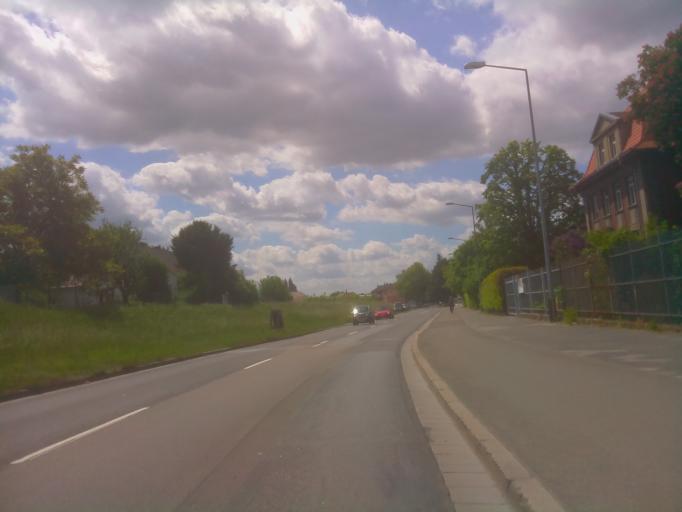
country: DE
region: Rheinland-Pfalz
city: Speyer
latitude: 49.3274
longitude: 8.4490
